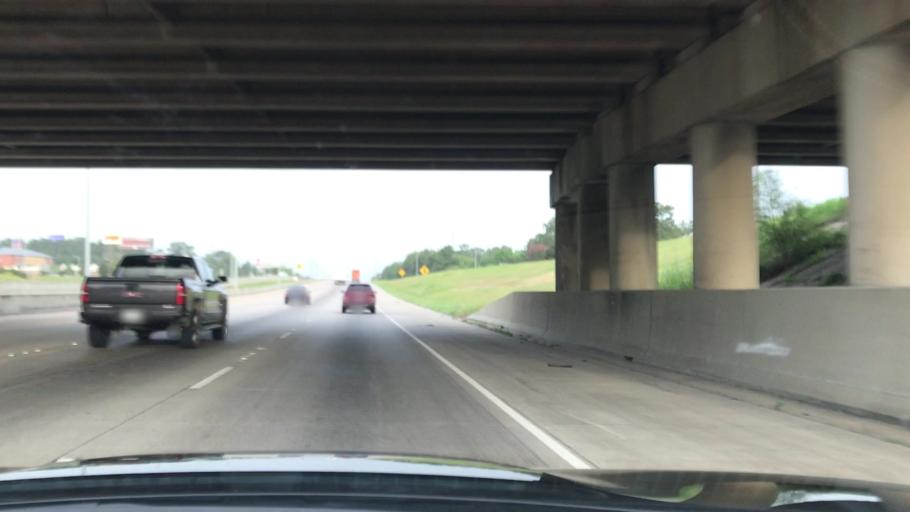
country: US
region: Louisiana
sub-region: Caddo Parish
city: Greenwood
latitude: 32.4507
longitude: -93.8654
